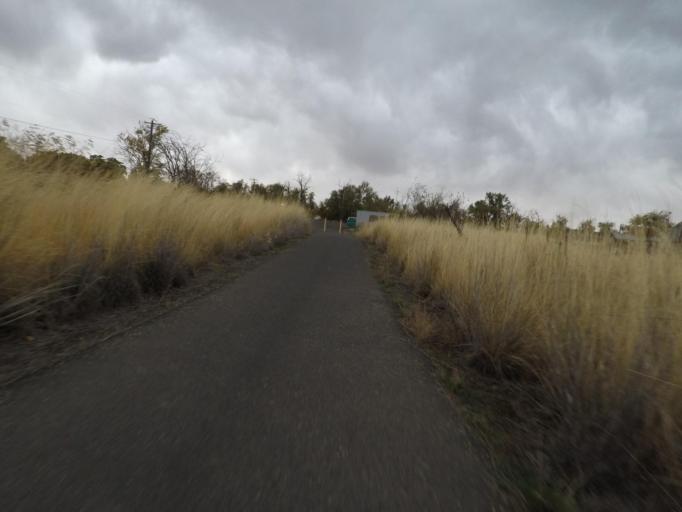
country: US
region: Washington
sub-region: Walla Walla County
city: Walla Walla East
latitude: 46.0754
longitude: -118.2719
